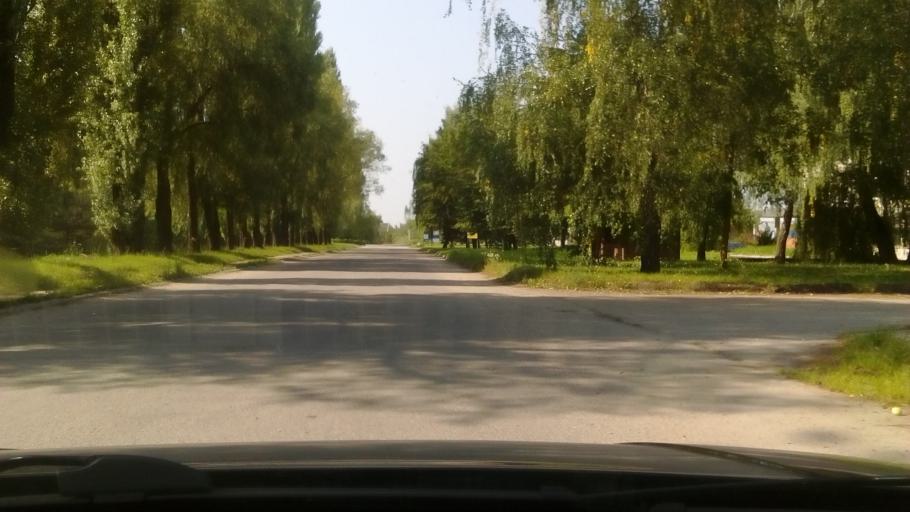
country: LT
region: Alytaus apskritis
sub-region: Alytus
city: Alytus
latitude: 54.4266
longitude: 24.0160
